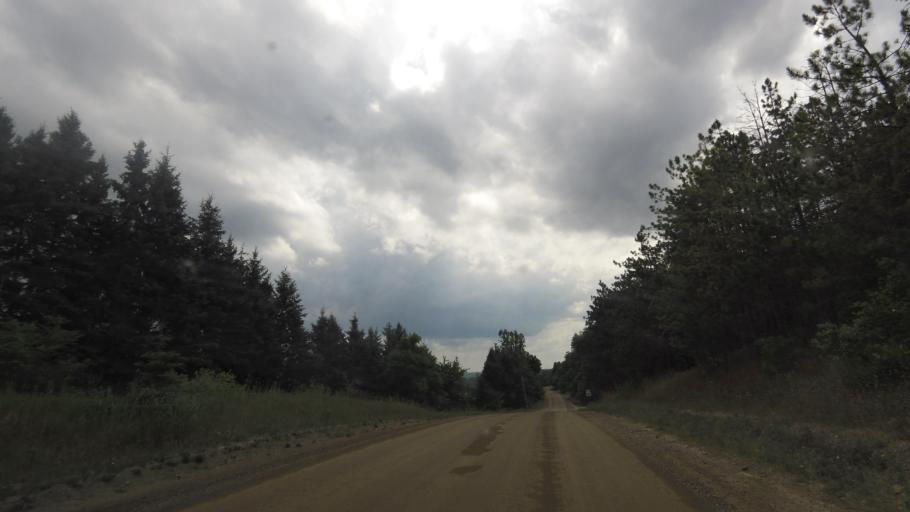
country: CA
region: Ontario
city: Orangeville
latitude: 43.8460
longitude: -79.9628
